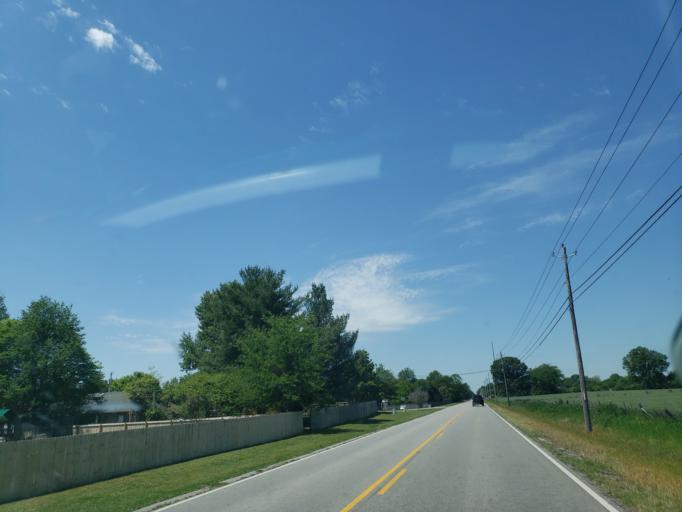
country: US
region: Alabama
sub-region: Madison County
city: Hazel Green
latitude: 34.9322
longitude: -86.5412
